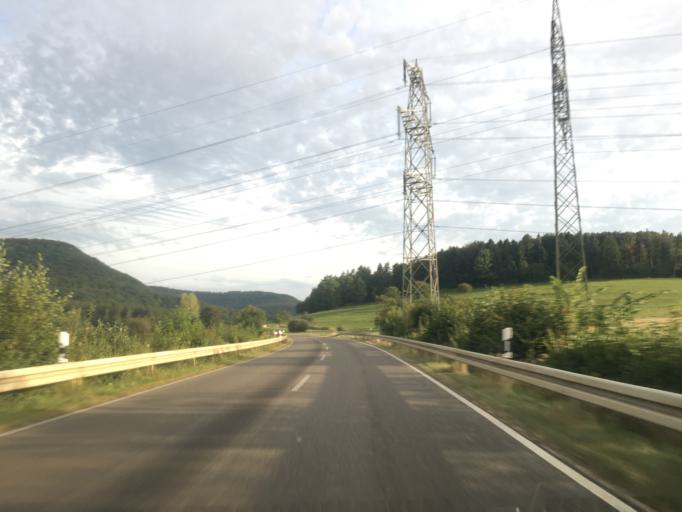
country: DE
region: Baden-Wuerttemberg
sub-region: Tuebingen Region
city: Eningen unter Achalm
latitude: 48.5051
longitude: 9.2667
